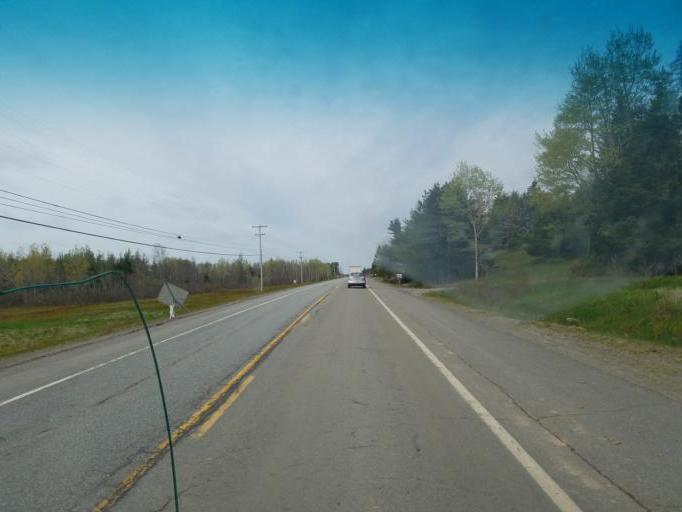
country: US
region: Maine
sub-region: Washington County
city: East Machias
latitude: 44.7636
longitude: -67.2099
